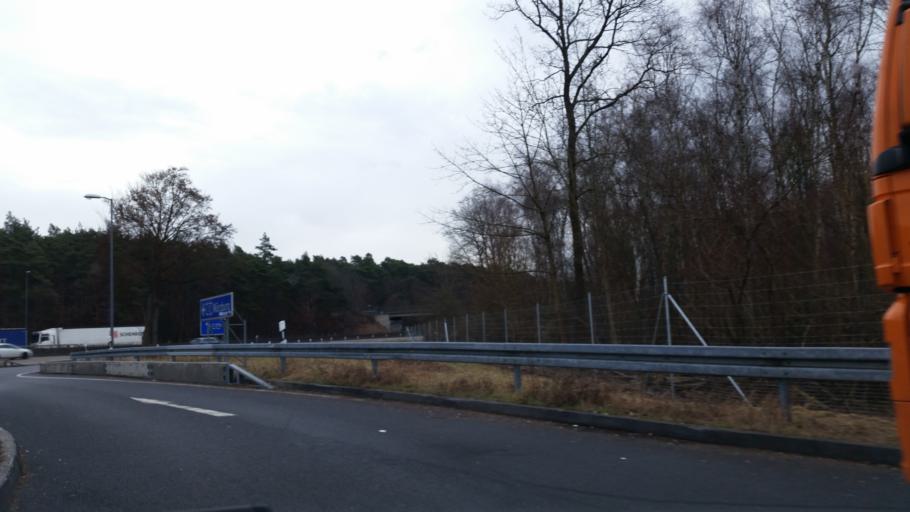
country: DE
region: Hesse
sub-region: Regierungsbezirk Darmstadt
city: Rodgau
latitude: 50.0543
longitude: 8.9102
